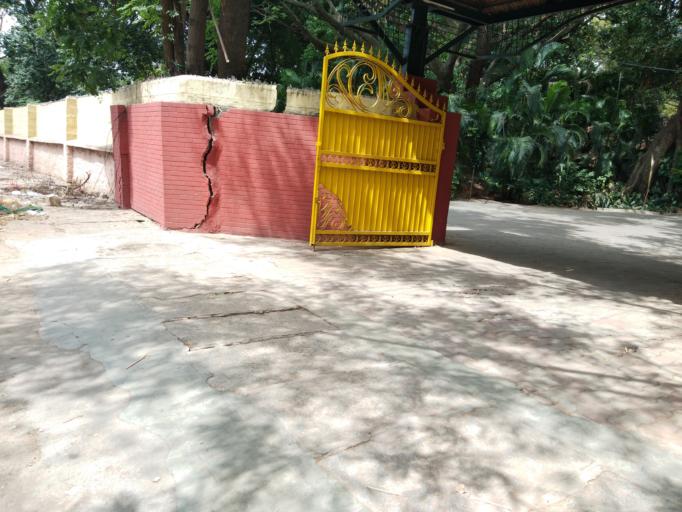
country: IN
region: Karnataka
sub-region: Bangalore Urban
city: Bangalore
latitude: 13.0048
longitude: 77.5935
